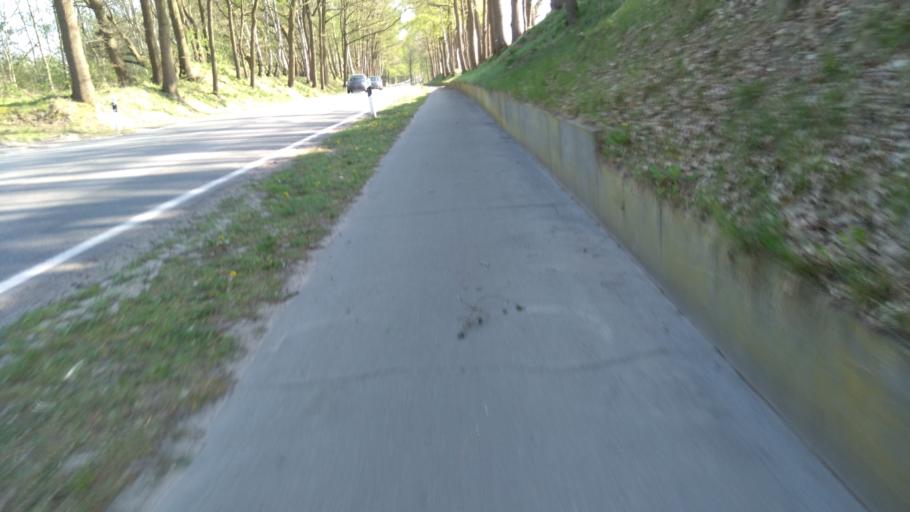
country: DE
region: Lower Saxony
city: Buxtehude
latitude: 53.4512
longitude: 9.6948
